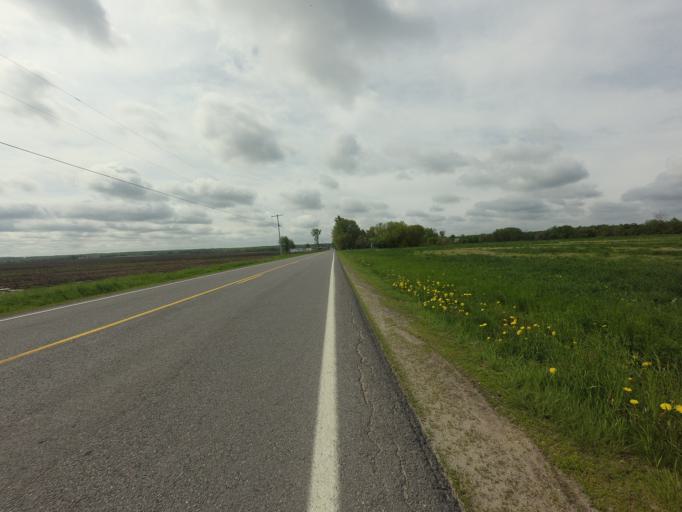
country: CA
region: Ontario
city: Cornwall
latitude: 44.7685
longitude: -74.6715
